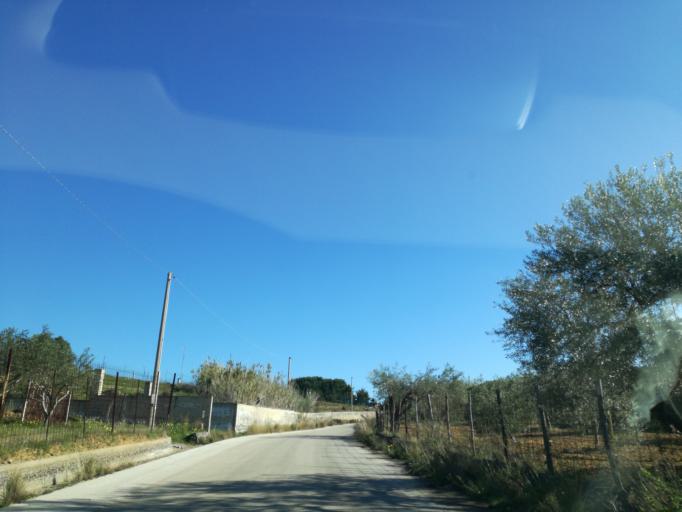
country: IT
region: Sicily
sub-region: Provincia di Caltanissetta
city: Niscemi
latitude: 37.0607
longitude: 14.3508
